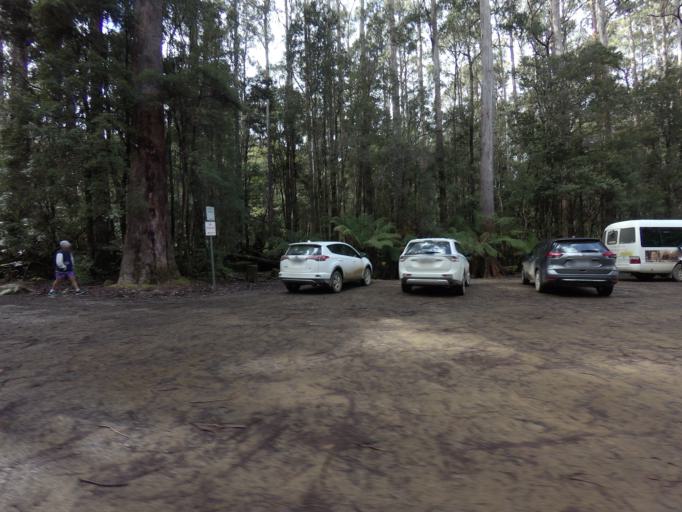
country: AU
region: Tasmania
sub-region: Huon Valley
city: Geeveston
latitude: -43.3822
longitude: 146.8418
